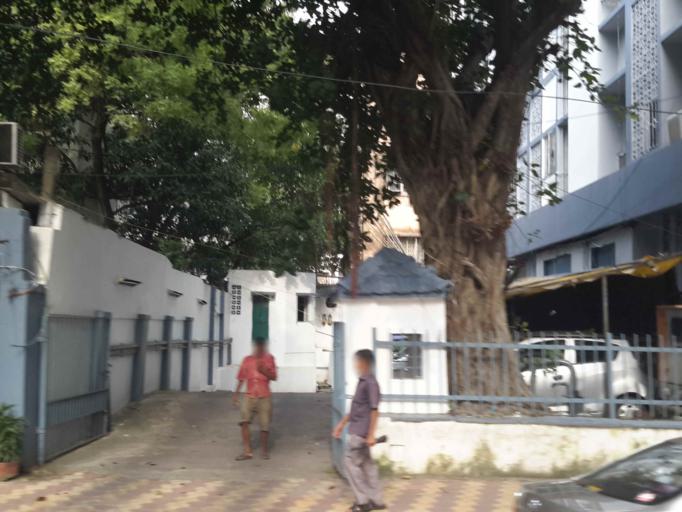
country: IN
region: West Bengal
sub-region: Kolkata
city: Kolkata
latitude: 22.5139
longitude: 88.3560
